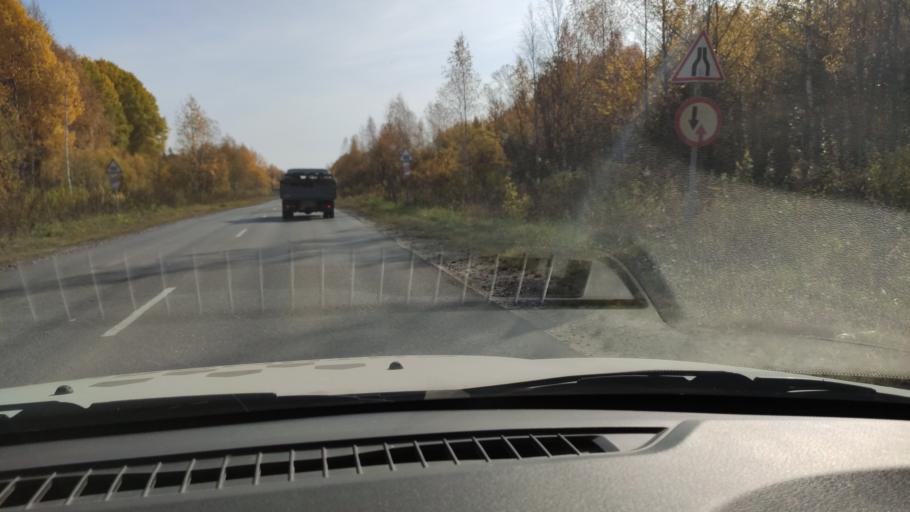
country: RU
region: Perm
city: Novyye Lyady
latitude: 58.0286
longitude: 56.6248
